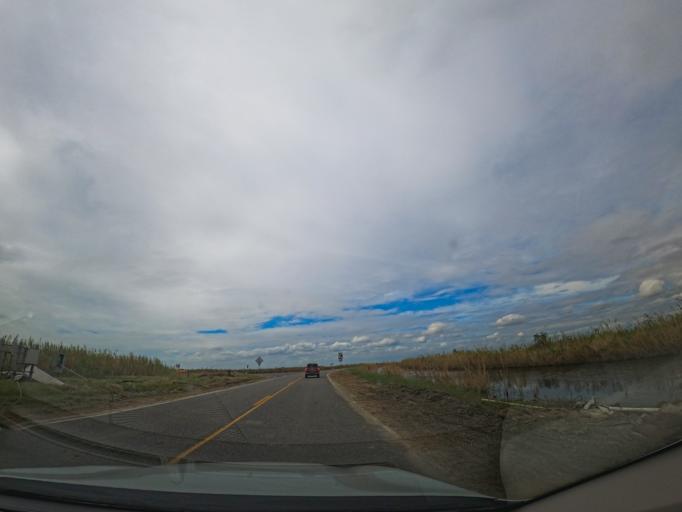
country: US
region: Louisiana
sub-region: Cameron Parish
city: Cameron
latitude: 29.7723
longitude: -93.4605
